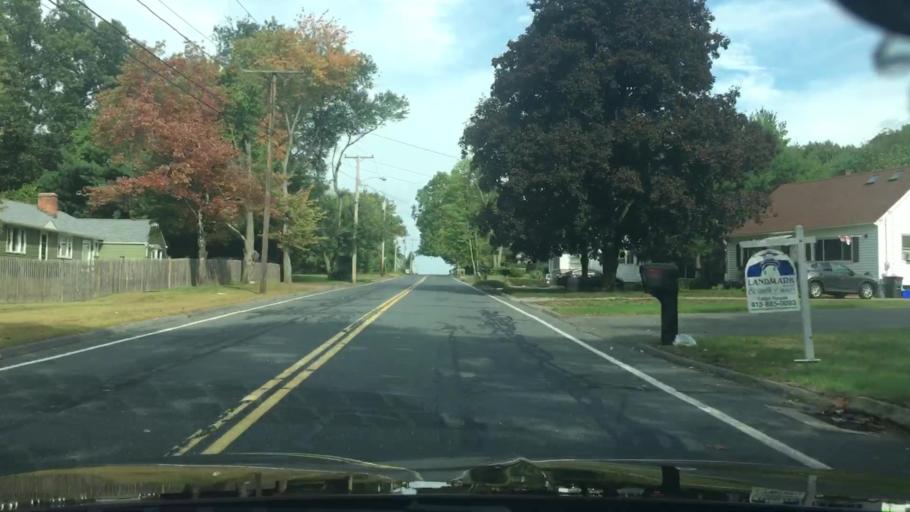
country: US
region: Massachusetts
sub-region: Hampden County
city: East Longmeadow
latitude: 42.0703
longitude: -72.5298
